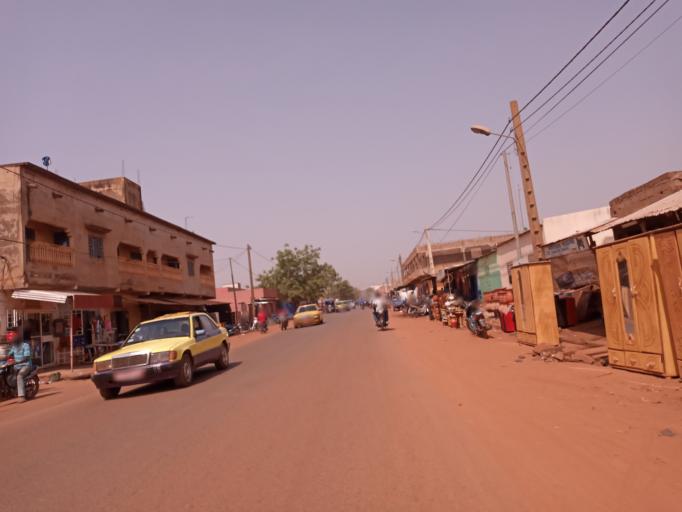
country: ML
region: Bamako
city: Bamako
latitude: 12.5888
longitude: -7.9834
